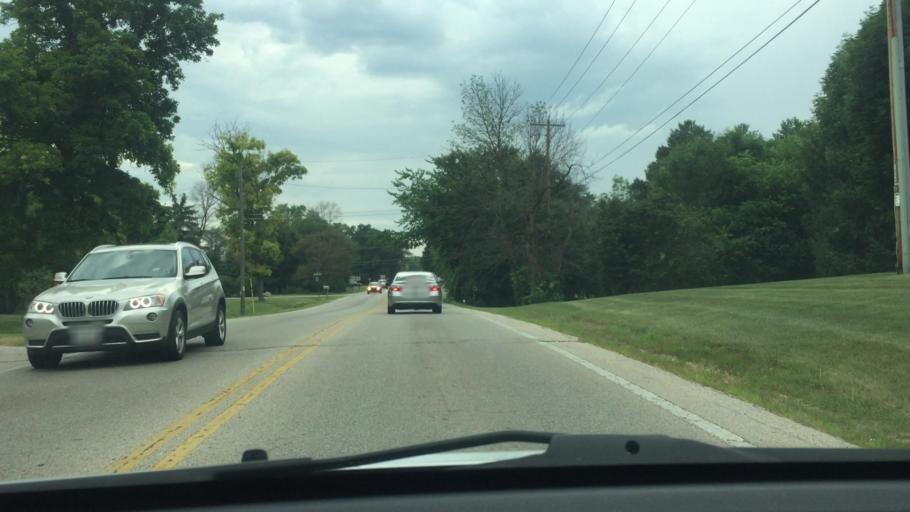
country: US
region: Wisconsin
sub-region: Waukesha County
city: Brookfield
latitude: 43.0605
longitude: -88.1034
